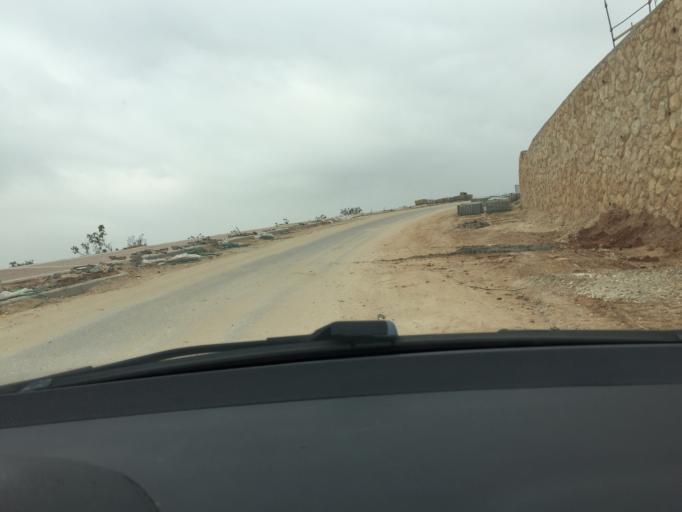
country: PS
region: West Bank
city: Rafat
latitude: 32.0661
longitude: 35.0483
